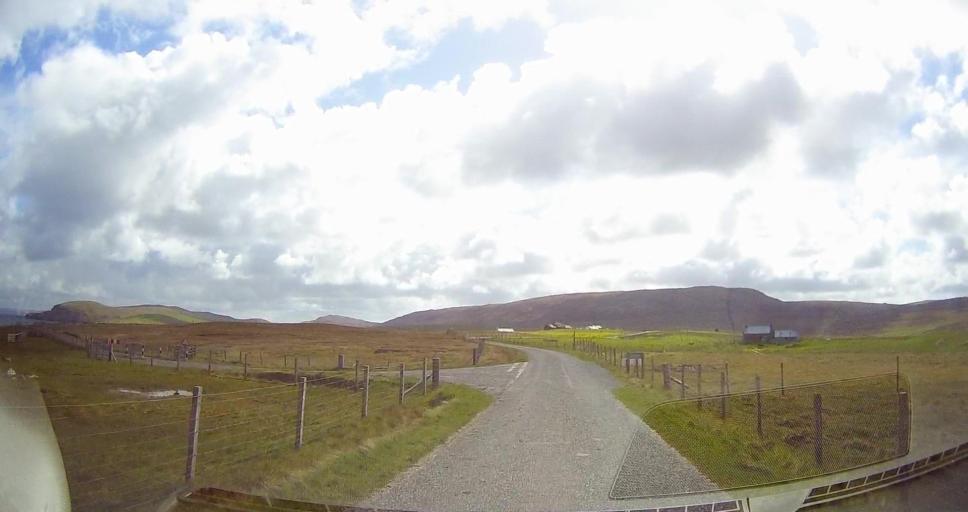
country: GB
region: Scotland
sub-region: Shetland Islands
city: Lerwick
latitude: 60.5911
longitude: -1.3284
